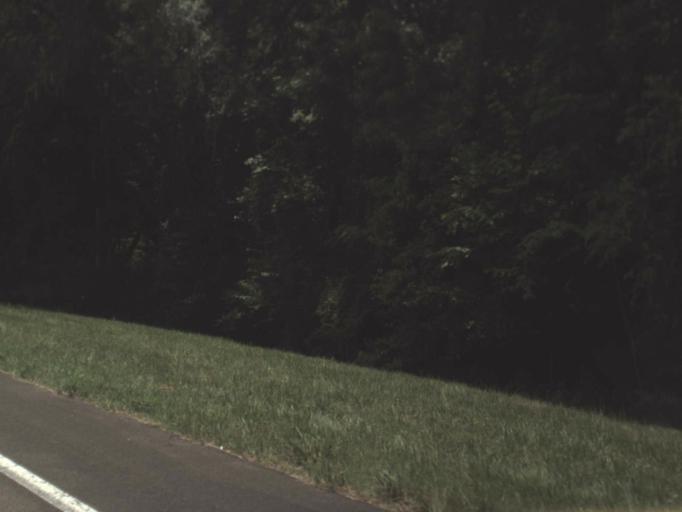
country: US
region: Florida
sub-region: Alachua County
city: Alachua
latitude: 29.8200
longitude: -82.3876
